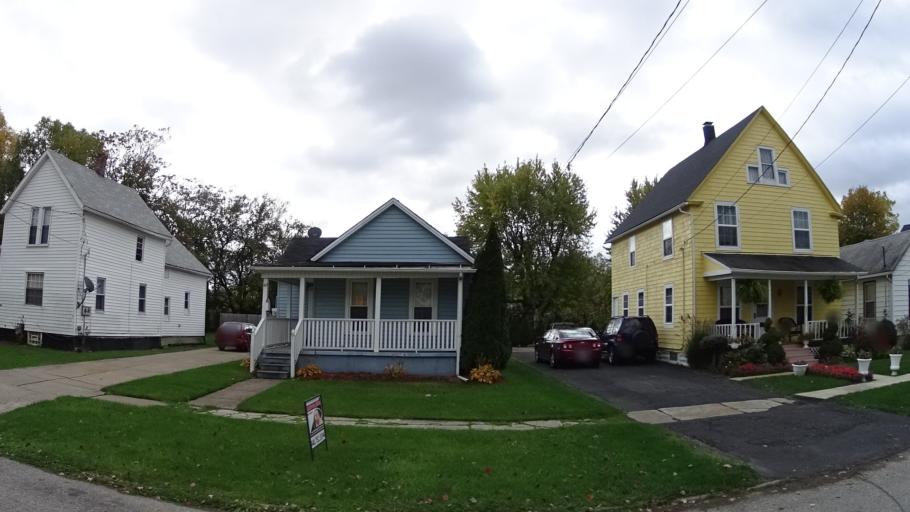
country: US
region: Ohio
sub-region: Lorain County
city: Lorain
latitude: 41.4501
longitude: -82.1709
